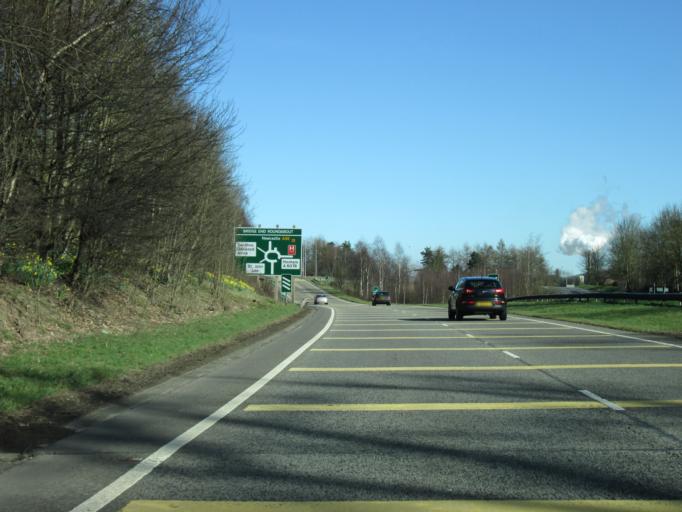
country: GB
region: England
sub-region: Northumberland
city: Hexham
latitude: 54.9821
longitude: -2.0985
